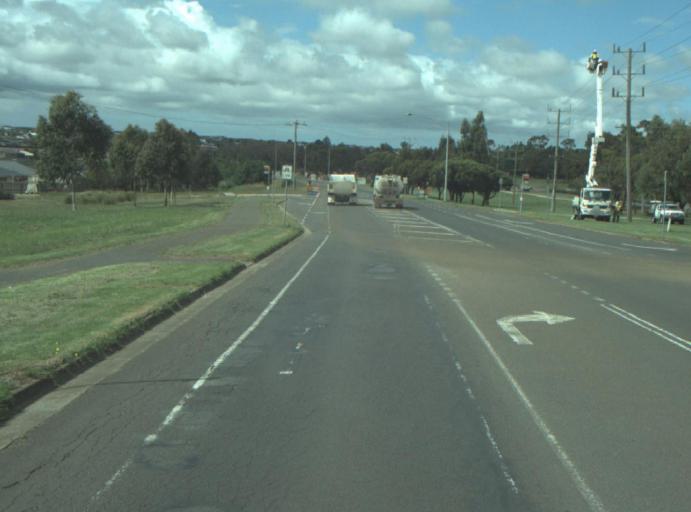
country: AU
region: Victoria
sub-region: Greater Geelong
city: Wandana Heights
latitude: -38.1952
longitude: 144.3050
